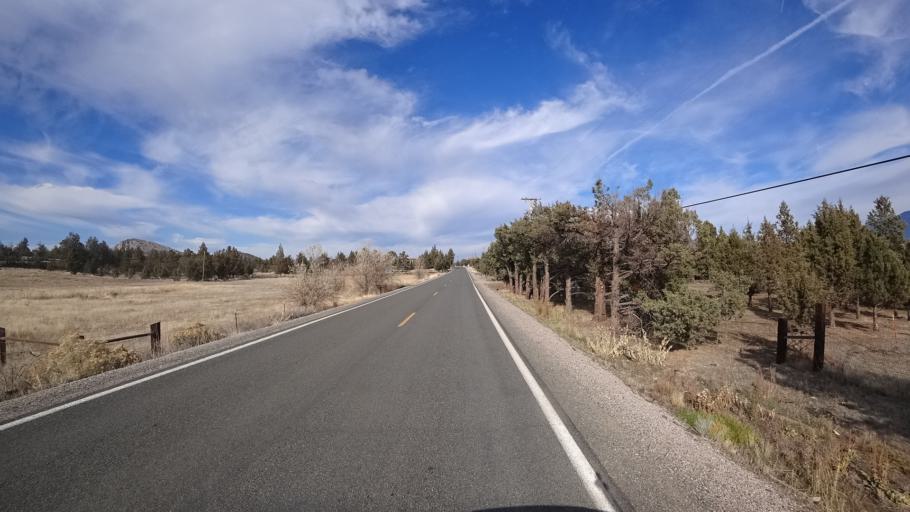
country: US
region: California
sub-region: Siskiyou County
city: Montague
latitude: 41.6448
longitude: -122.3987
